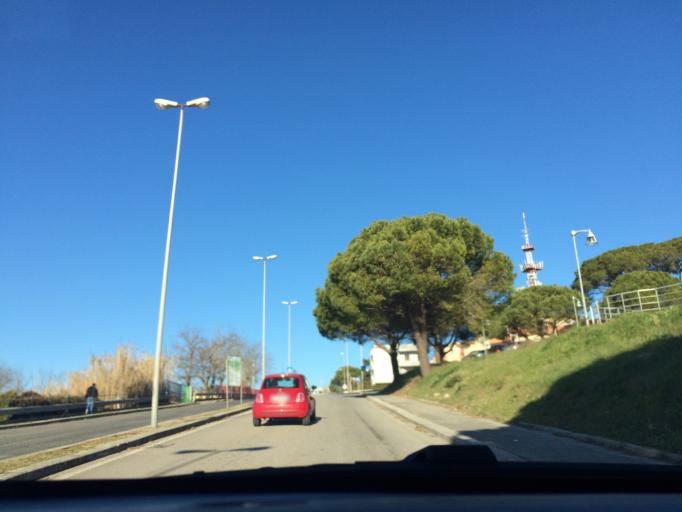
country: IT
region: Basilicate
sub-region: Provincia di Matera
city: Matera
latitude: 40.6574
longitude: 16.6104
